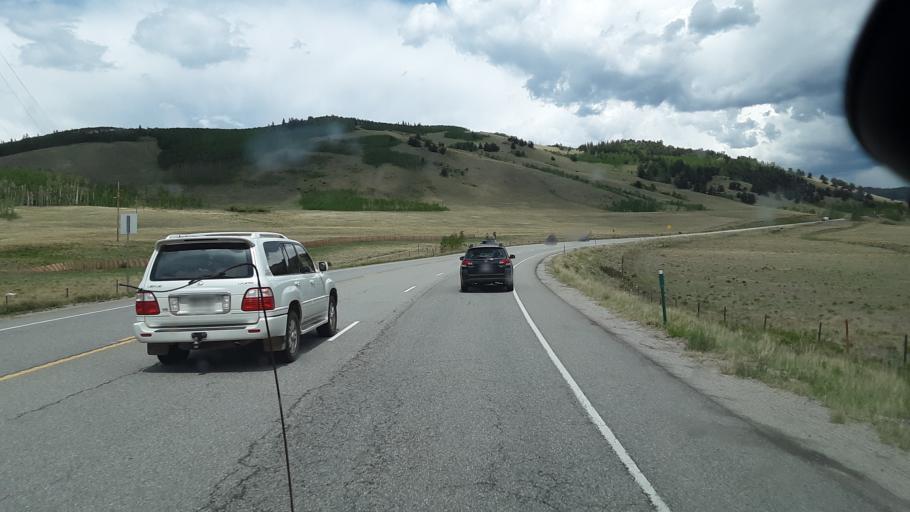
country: US
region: Colorado
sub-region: Summit County
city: Breckenridge
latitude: 39.4064
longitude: -105.7743
